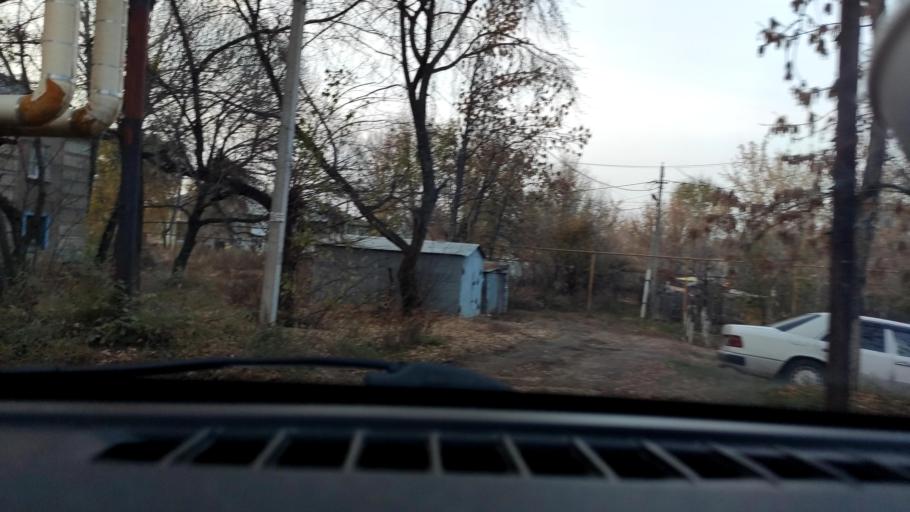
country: RU
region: Samara
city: Samara
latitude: 53.1490
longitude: 50.1385
